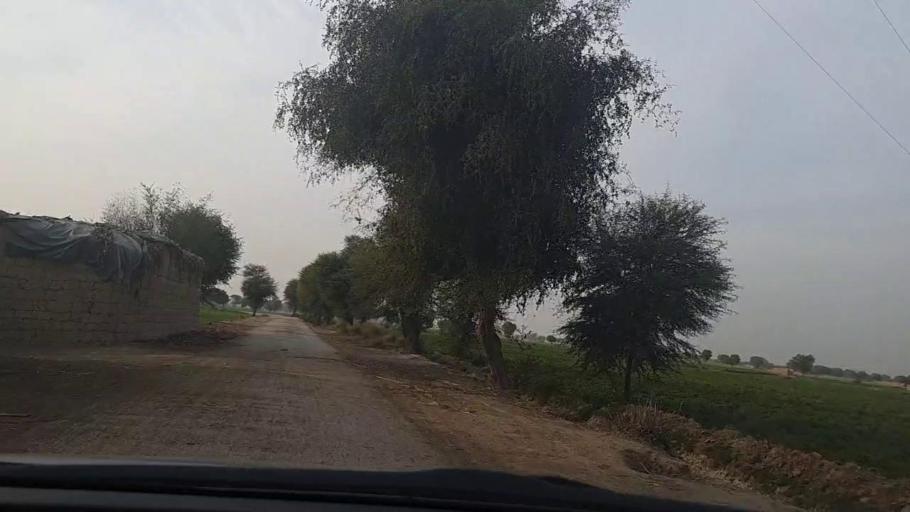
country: PK
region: Sindh
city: Daulatpur
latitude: 26.3358
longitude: 68.0380
